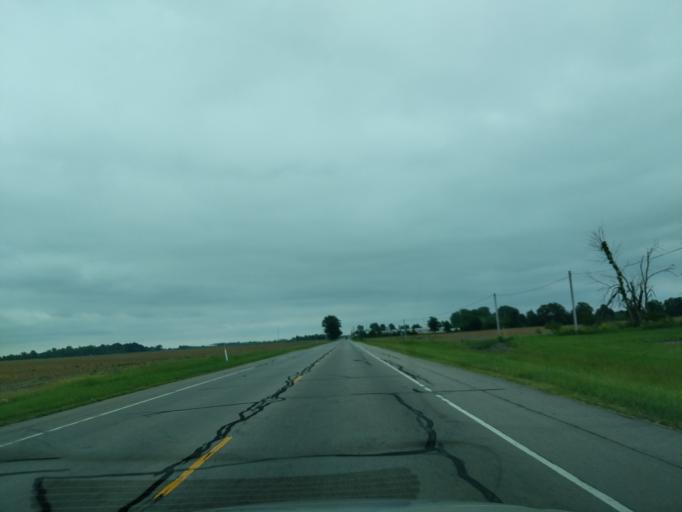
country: US
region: Indiana
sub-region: Madison County
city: Alexandria
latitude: 40.2772
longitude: -85.5725
